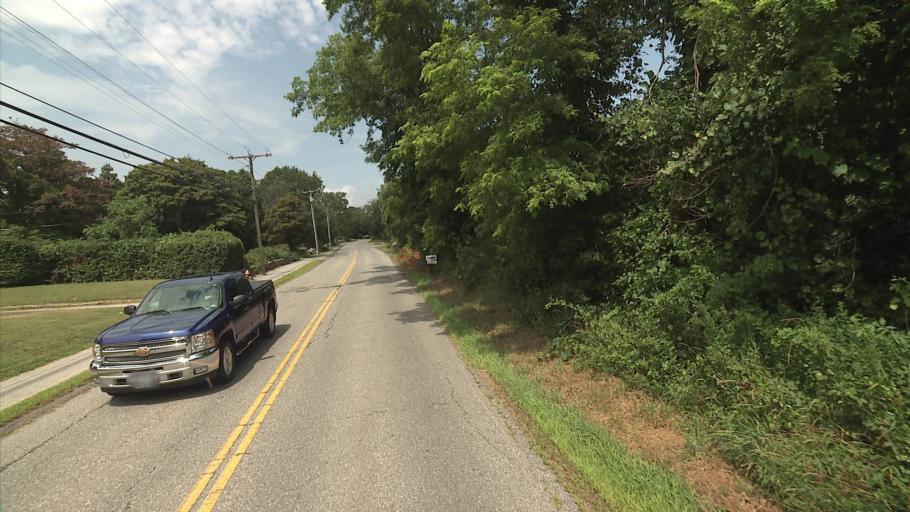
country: US
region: Connecticut
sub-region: New London County
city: Central Waterford
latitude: 41.3168
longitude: -72.1331
